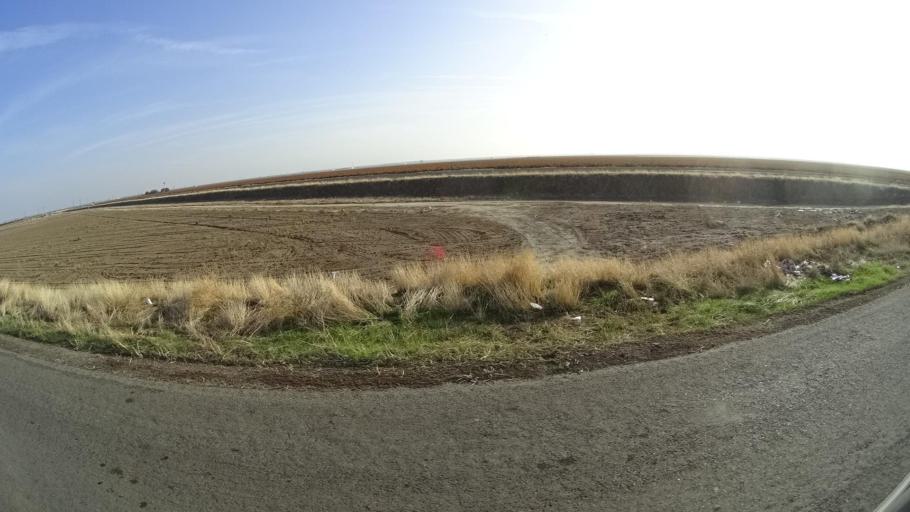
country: US
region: California
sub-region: Kern County
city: McFarland
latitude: 35.7127
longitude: -119.1872
